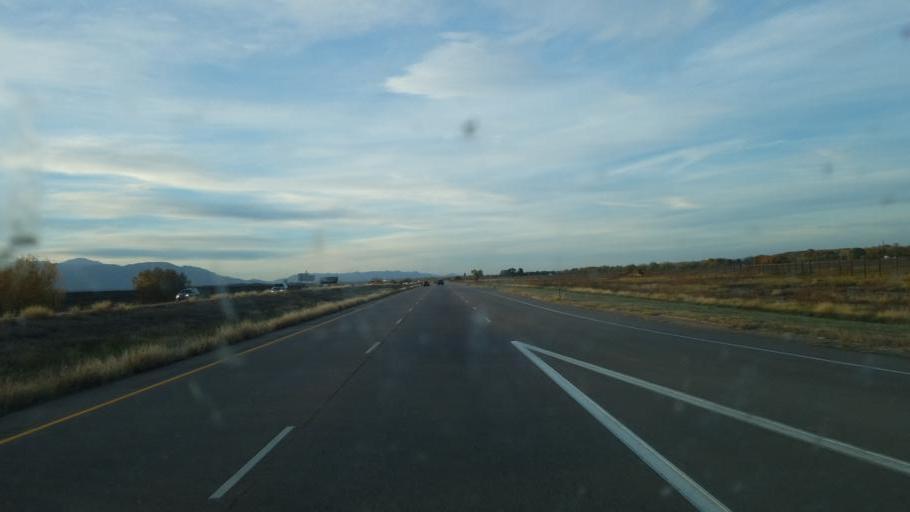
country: US
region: Colorado
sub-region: El Paso County
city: Fountain
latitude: 38.5895
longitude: -104.6707
